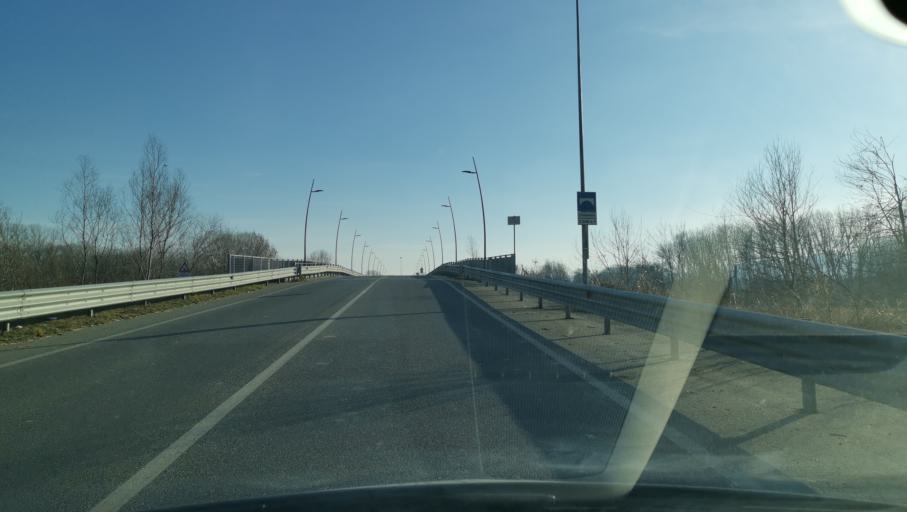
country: IT
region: Piedmont
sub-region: Provincia di Torino
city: Pavone Canavese
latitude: 45.4236
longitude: 7.8591
